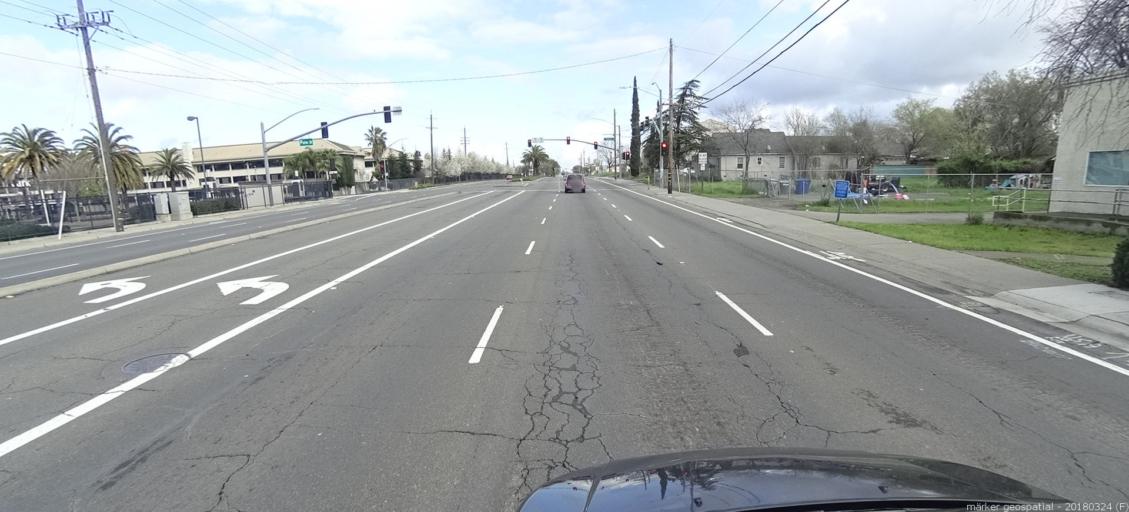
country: US
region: California
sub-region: Sacramento County
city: North Highlands
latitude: 38.6648
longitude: -121.3828
